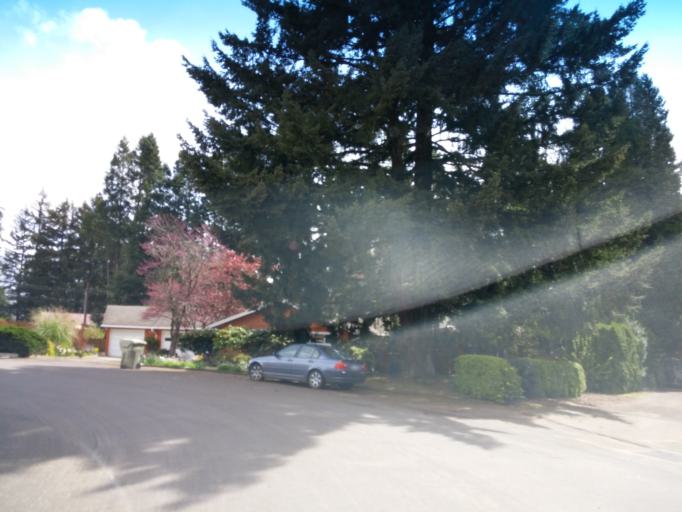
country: US
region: Oregon
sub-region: Washington County
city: Cedar Hills
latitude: 45.5142
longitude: -122.8003
